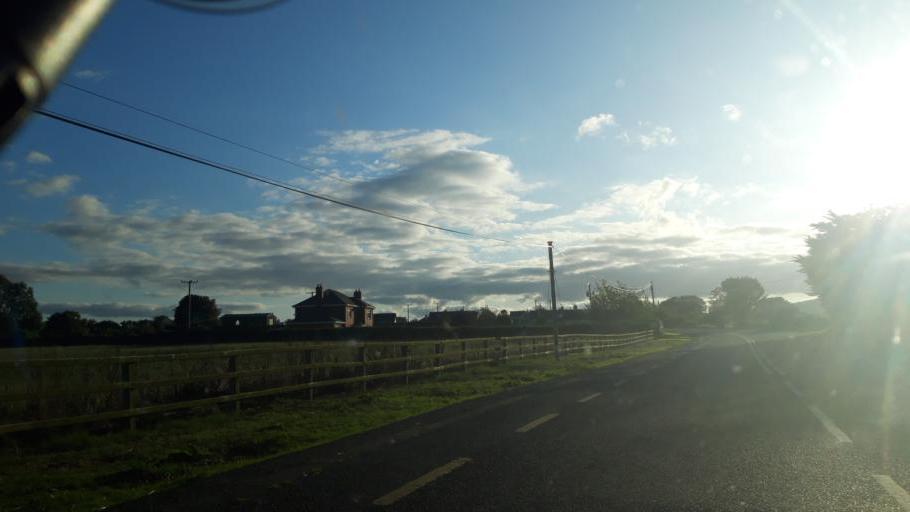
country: IE
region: Leinster
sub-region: Lu
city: Carlingford
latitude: 54.0169
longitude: -6.1524
